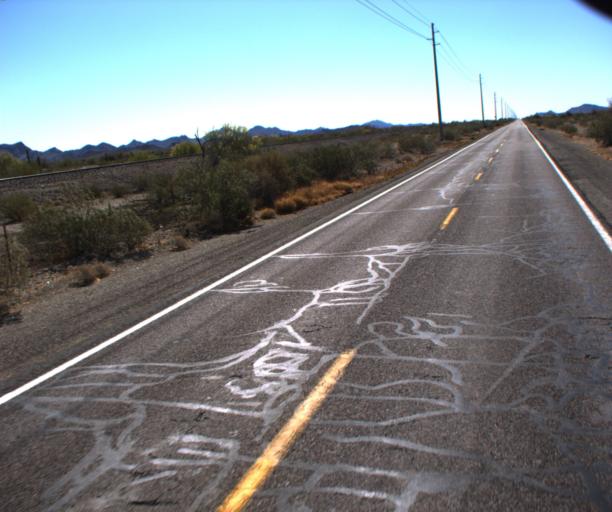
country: US
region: Arizona
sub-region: La Paz County
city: Salome
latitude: 33.7878
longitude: -113.8166
